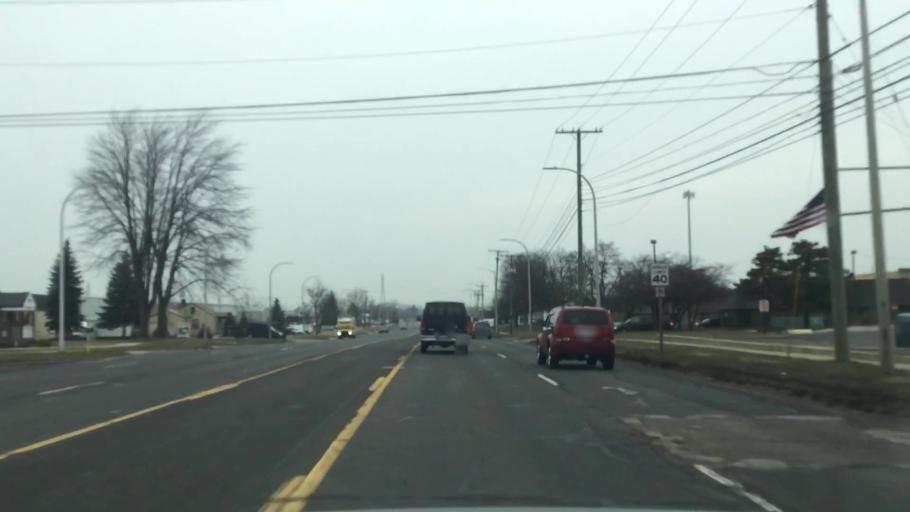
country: US
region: Michigan
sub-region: Wayne County
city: Livonia
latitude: 42.3707
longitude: -83.3525
